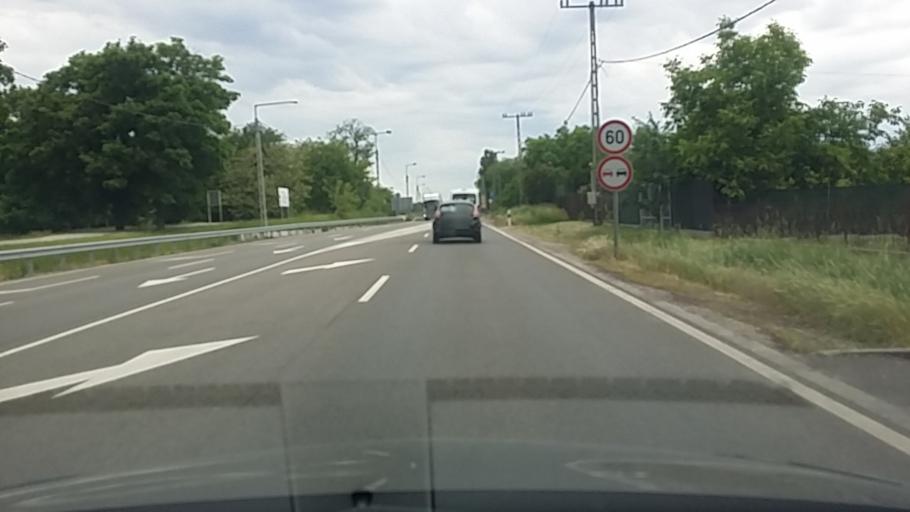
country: HU
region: Fejer
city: dunaujvaros
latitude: 46.9813
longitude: 18.9097
